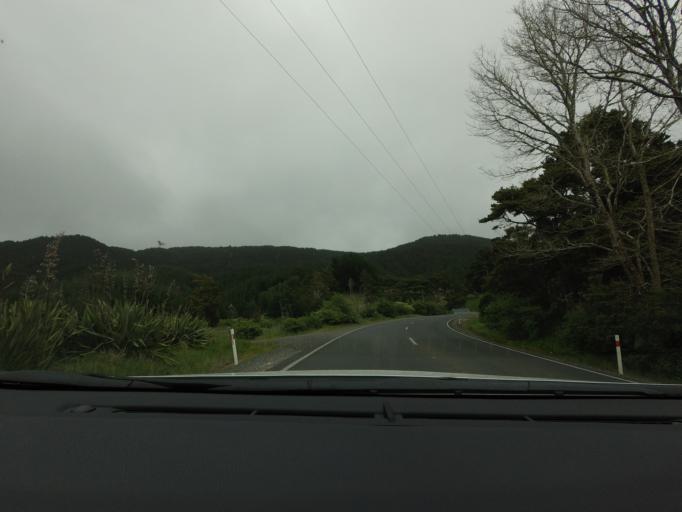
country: NZ
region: Auckland
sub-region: Auckland
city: Wellsford
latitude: -36.2944
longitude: 174.6166
